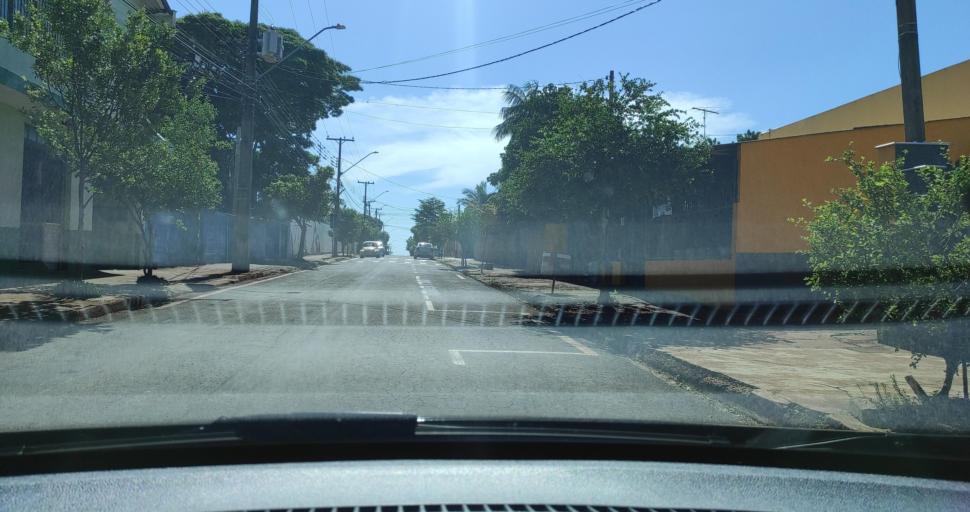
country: BR
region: Parana
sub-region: Ibipora
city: Ibipora
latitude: -23.2604
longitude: -51.0581
